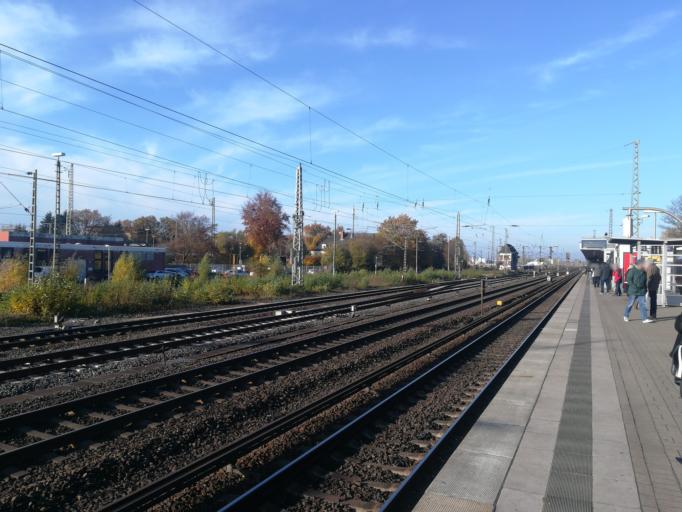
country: DE
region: Hamburg
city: Eidelstedt
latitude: 53.6021
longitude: 9.8944
